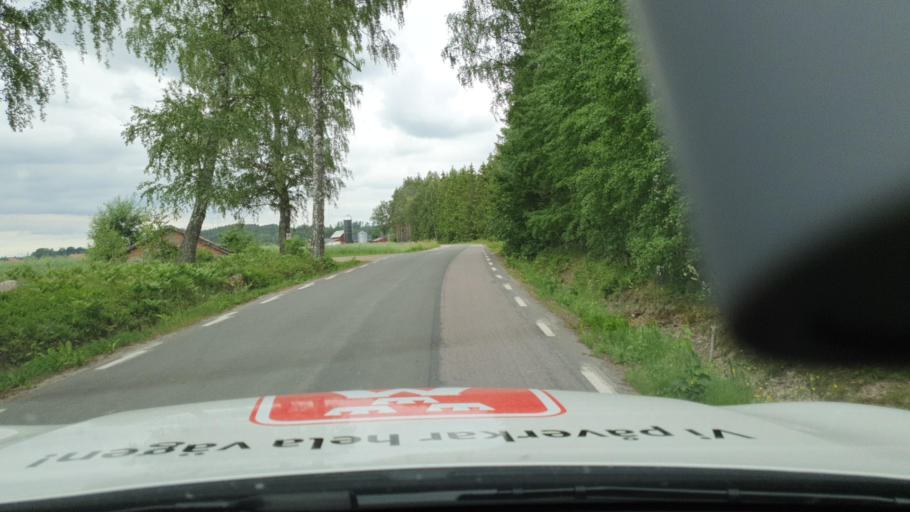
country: SE
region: Vaestra Goetaland
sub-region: Tidaholms Kommun
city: Olofstorp
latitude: 58.2866
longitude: 14.1020
